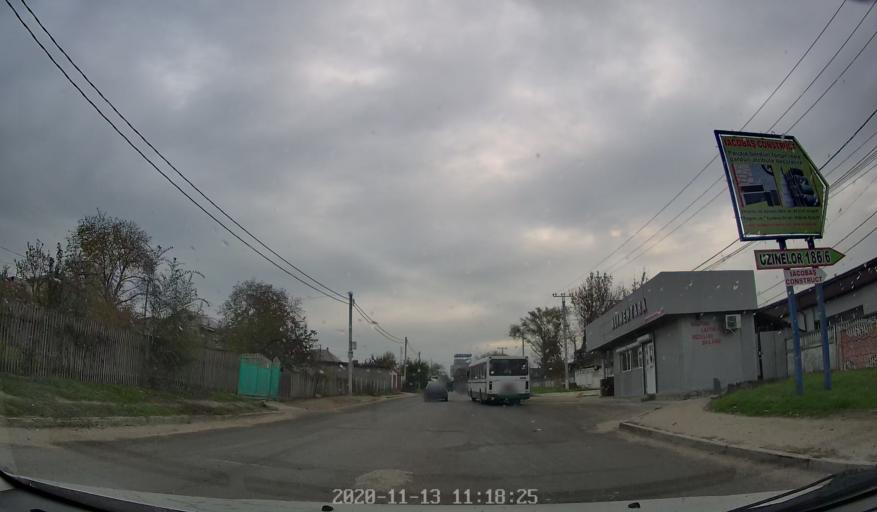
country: MD
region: Chisinau
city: Chisinau
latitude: 46.9909
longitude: 28.9126
